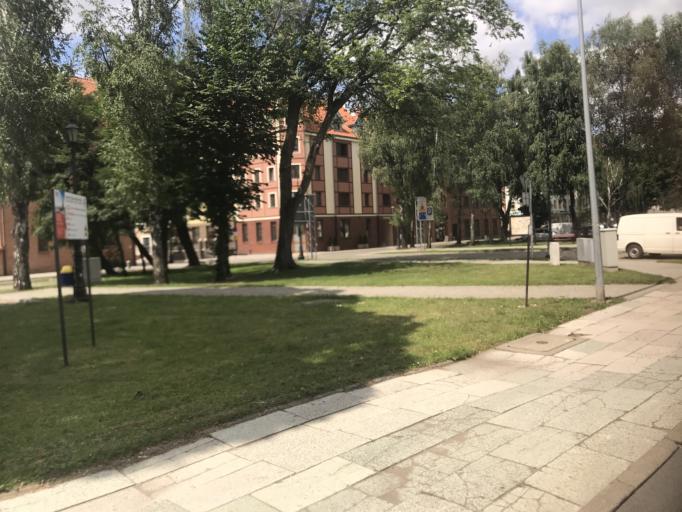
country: PL
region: Warmian-Masurian Voivodeship
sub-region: Powiat elblaski
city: Elblag
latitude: 54.1578
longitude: 19.3985
